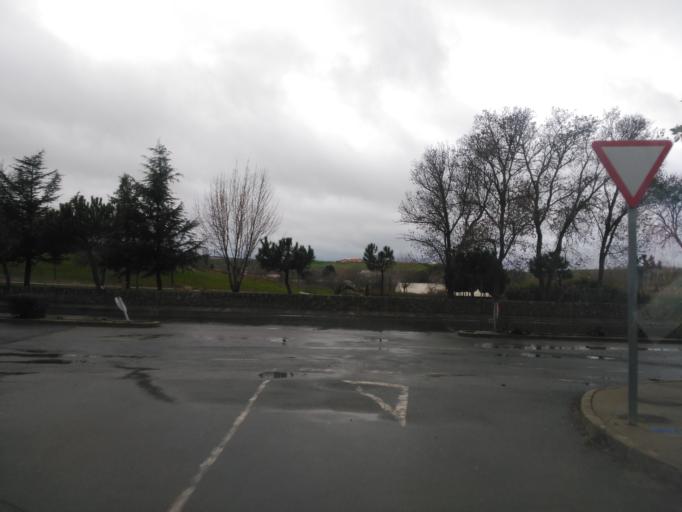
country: ES
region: Castille and Leon
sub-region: Provincia de Salamanca
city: Villamayor
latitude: 40.9823
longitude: -5.7104
